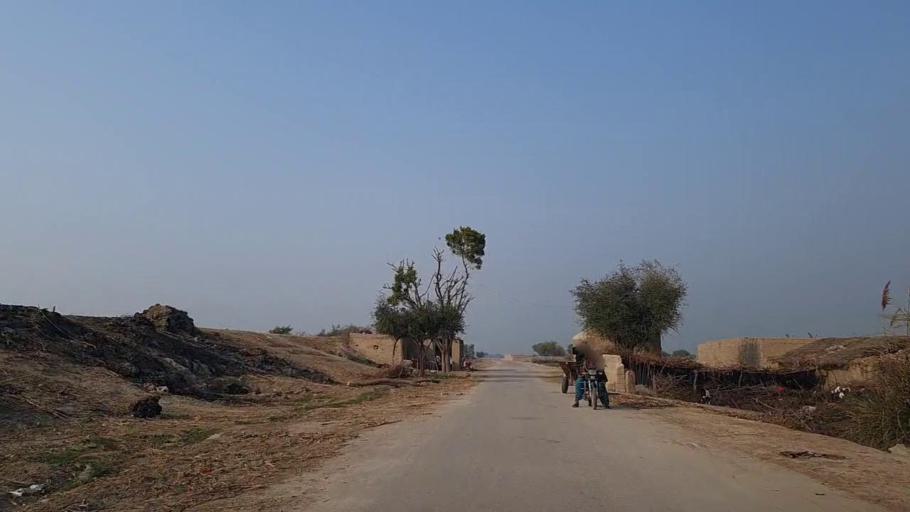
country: PK
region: Sindh
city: Sann
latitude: 26.1119
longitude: 68.1502
